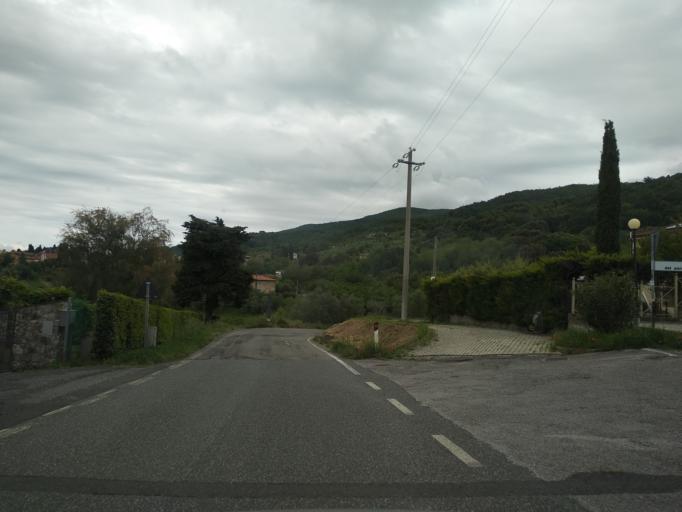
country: IT
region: Tuscany
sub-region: Provincia di Livorno
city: Collesalvetti
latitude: 43.5415
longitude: 10.4401
